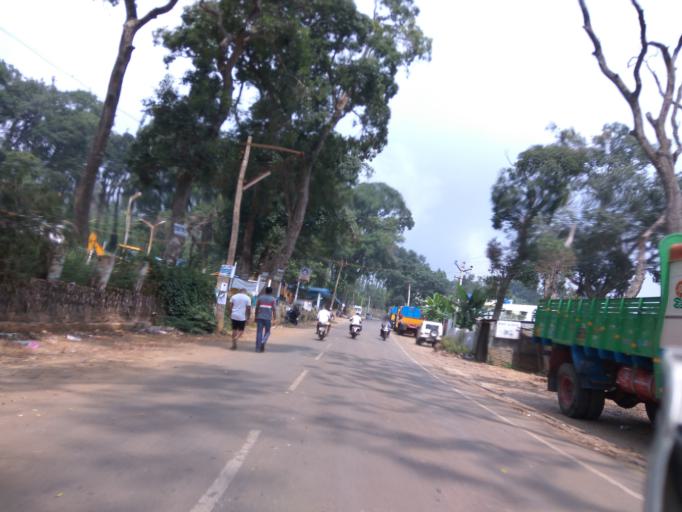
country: IN
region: Tamil Nadu
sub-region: Salem
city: Salem
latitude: 11.7864
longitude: 78.2110
